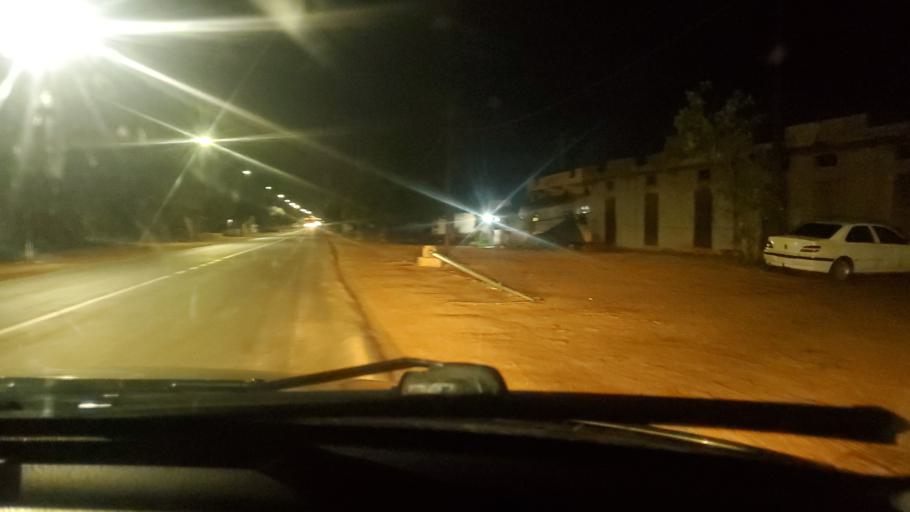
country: SN
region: Louga
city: Gueoul
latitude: 15.3663
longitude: -16.4532
